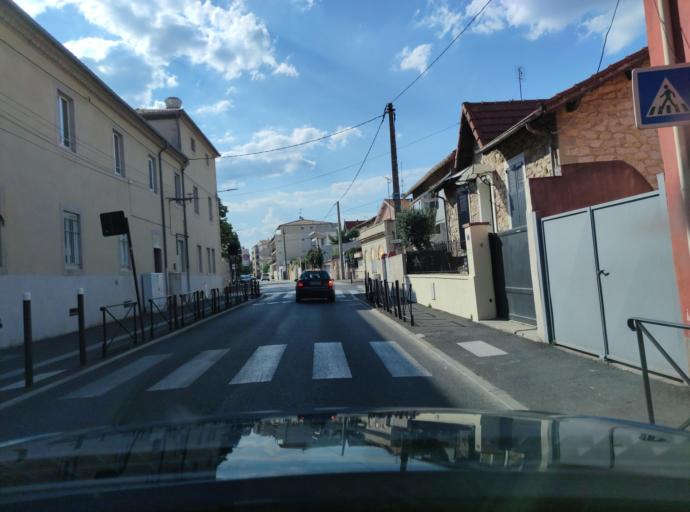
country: FR
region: Languedoc-Roussillon
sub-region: Departement du Gard
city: Nimes
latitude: 43.8355
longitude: 4.3755
